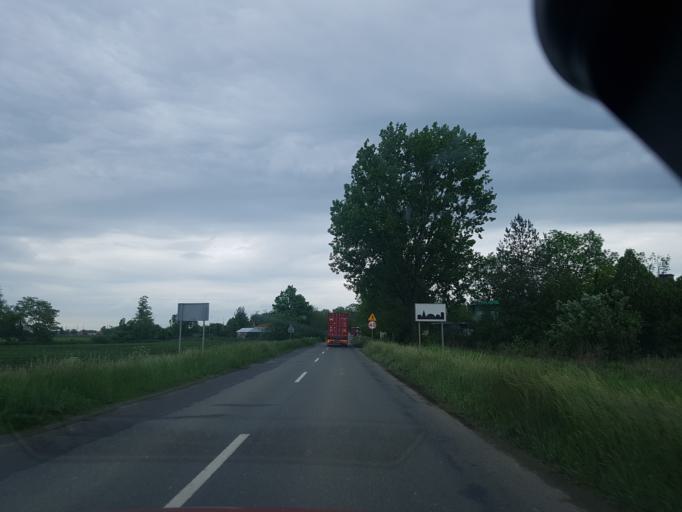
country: PL
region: Lower Silesian Voivodeship
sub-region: Powiat wroclawski
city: Zorawina
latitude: 50.9256
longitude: 17.0295
